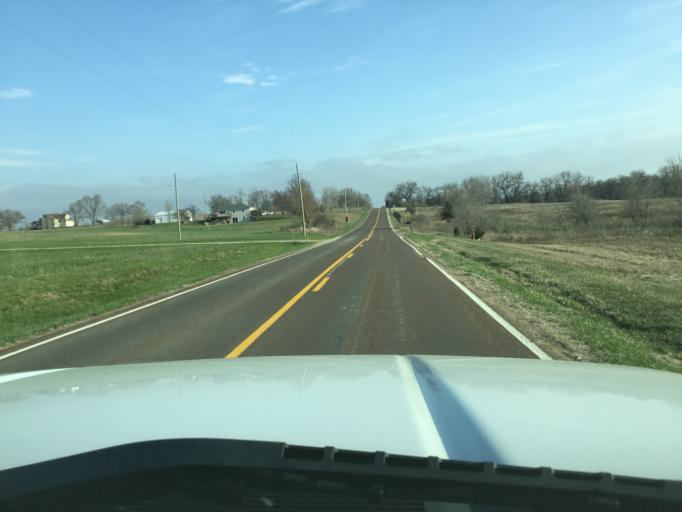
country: US
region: Kansas
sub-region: Shawnee County
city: Topeka
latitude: 39.1206
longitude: -95.7530
